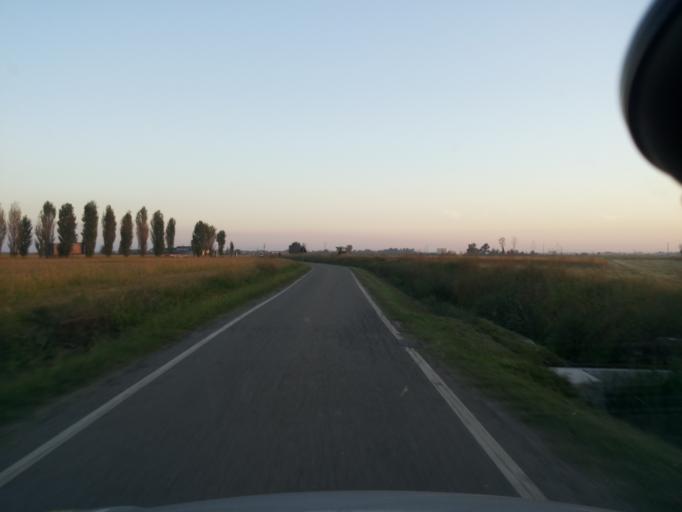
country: IT
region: Piedmont
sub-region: Provincia di Vercelli
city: San Germano Vercellese
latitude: 45.3689
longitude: 8.2410
